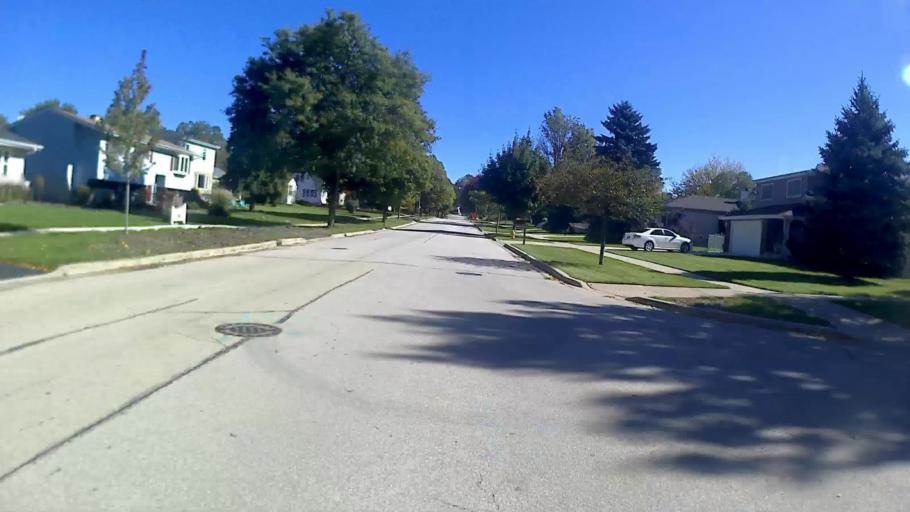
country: US
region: Illinois
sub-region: DuPage County
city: Lombard
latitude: 41.9006
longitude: -88.0132
